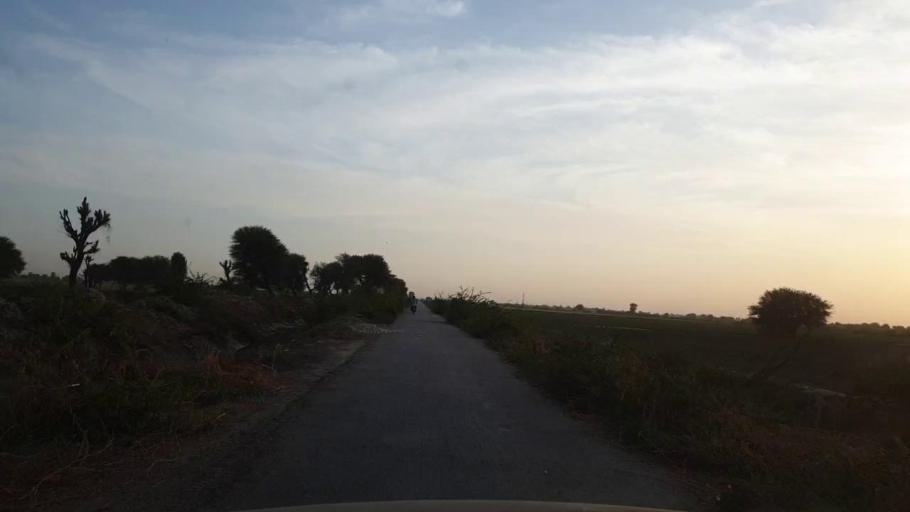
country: PK
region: Sindh
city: Kunri
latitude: 25.1297
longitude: 69.5724
